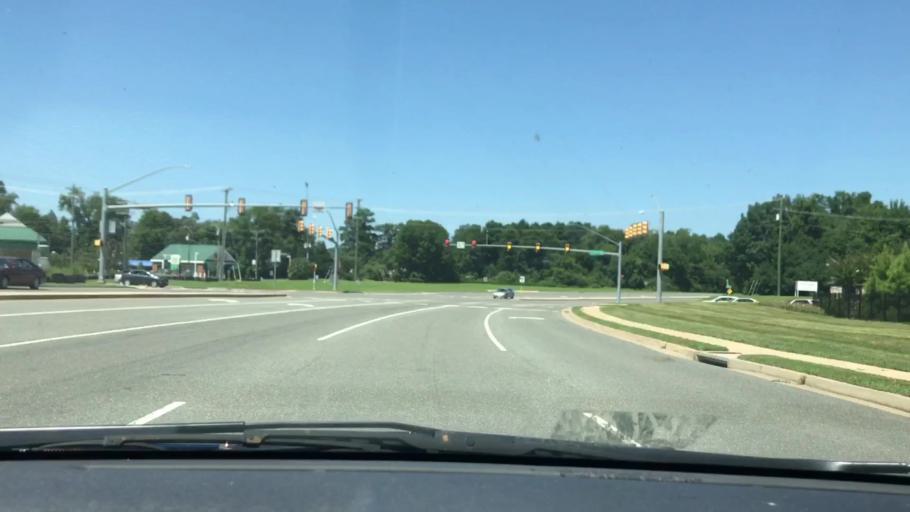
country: US
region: Virginia
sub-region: Henrico County
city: Short Pump
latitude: 37.6325
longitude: -77.6124
